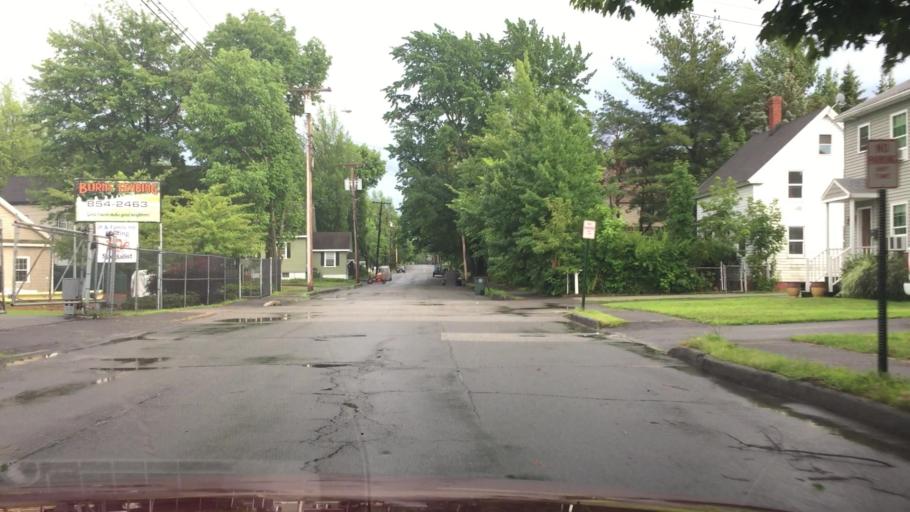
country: US
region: Maine
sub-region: Cumberland County
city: Westbrook
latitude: 43.6799
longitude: -70.3522
